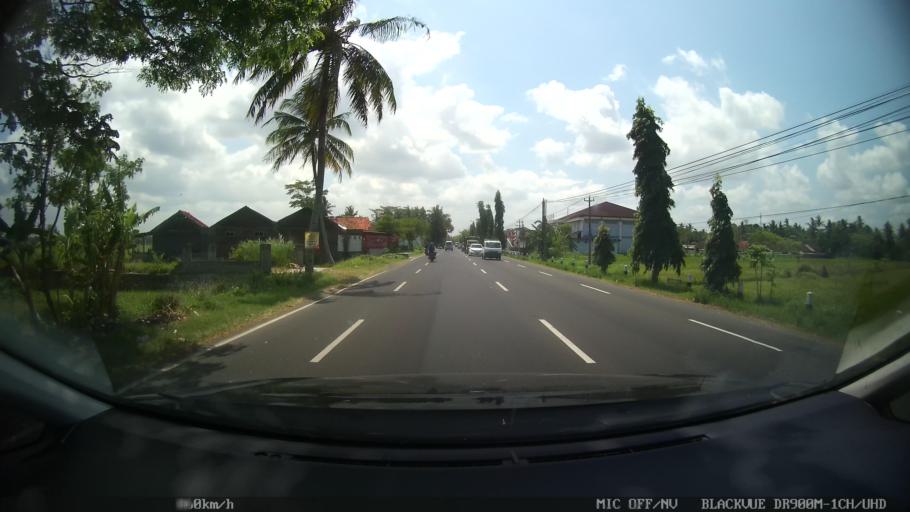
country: ID
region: Daerah Istimewa Yogyakarta
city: Pandak
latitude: -7.9201
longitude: 110.2825
